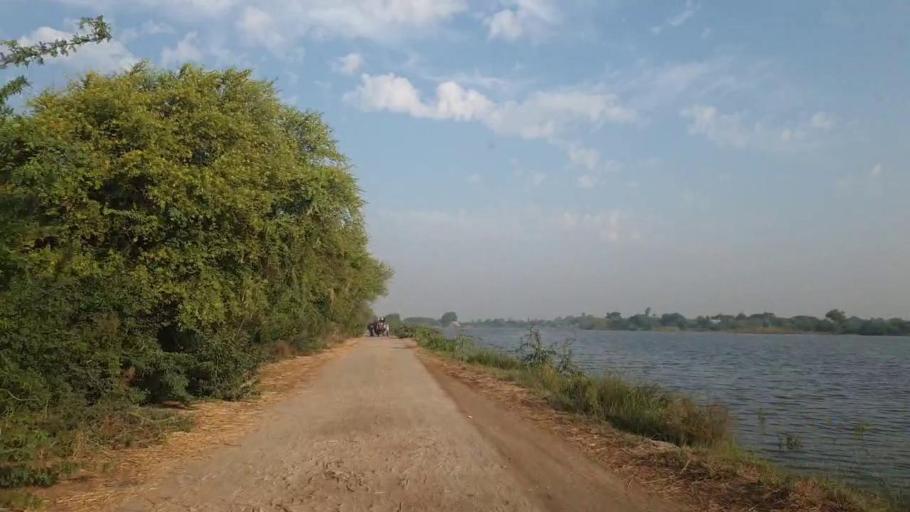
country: PK
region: Sindh
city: Tando Bago
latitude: 24.7991
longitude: 68.9604
